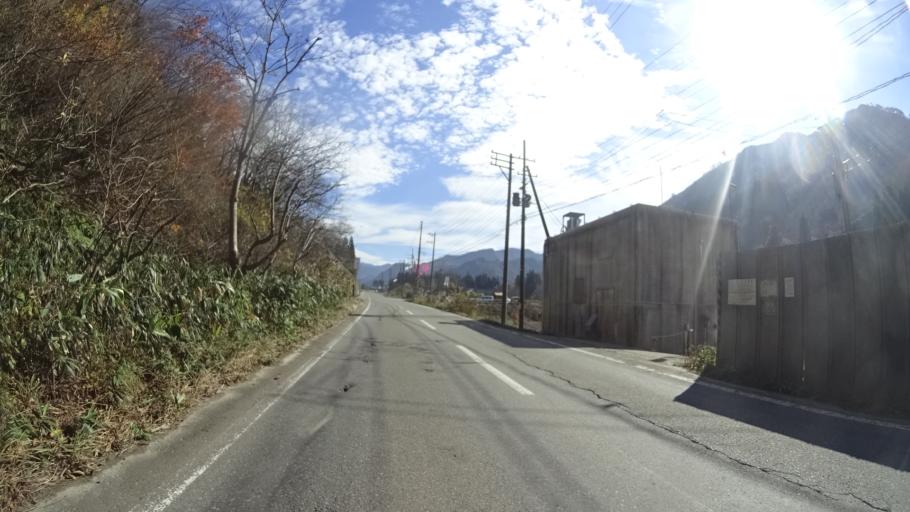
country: JP
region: Niigata
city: Muikamachi
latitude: 37.2218
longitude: 139.0277
